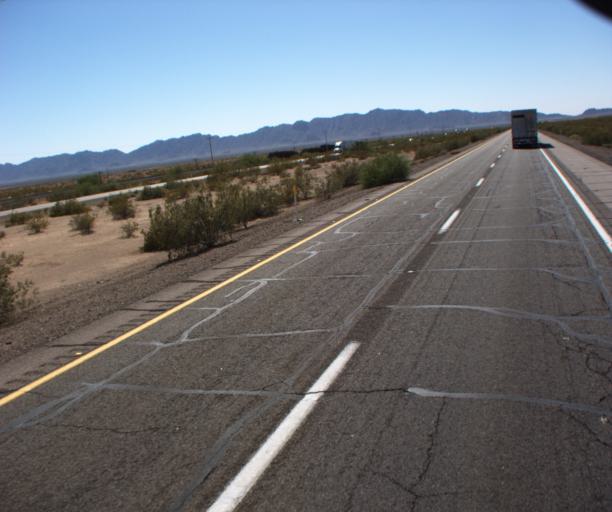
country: US
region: Arizona
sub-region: Yuma County
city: Wellton
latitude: 32.7633
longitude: -113.6293
